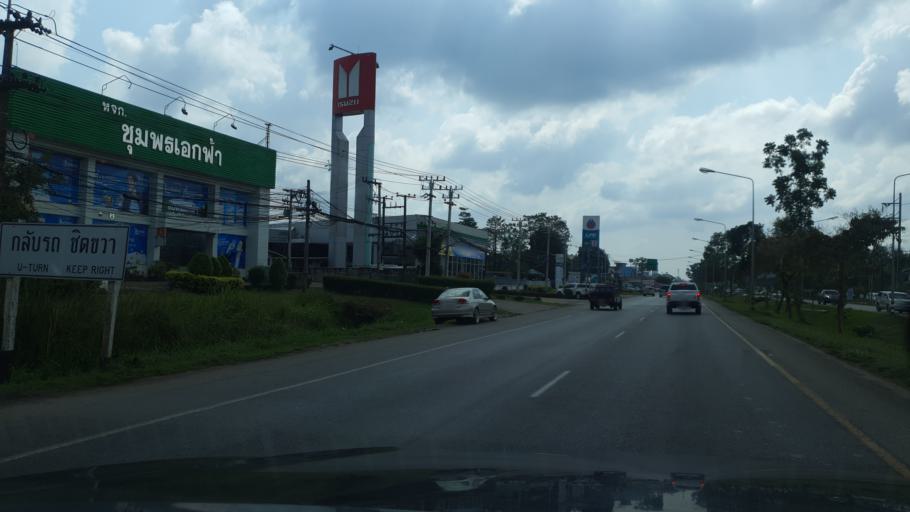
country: TH
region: Chumphon
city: Chumphon
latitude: 10.5031
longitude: 99.1183
